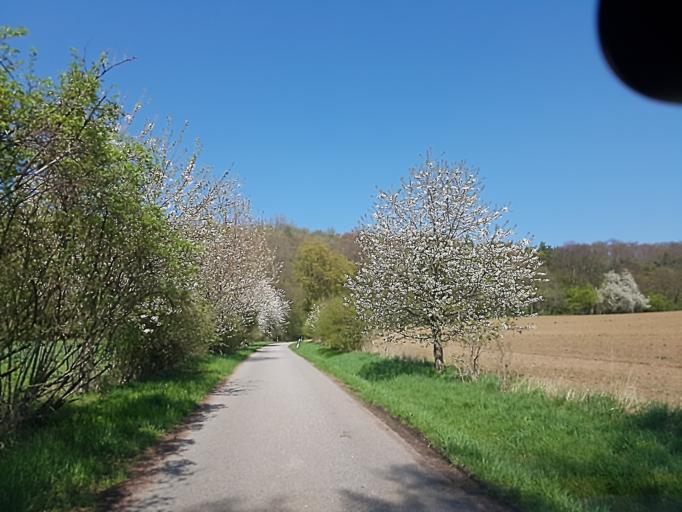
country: DE
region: Saxony
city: Bockelwitz
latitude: 51.1580
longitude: 12.9893
